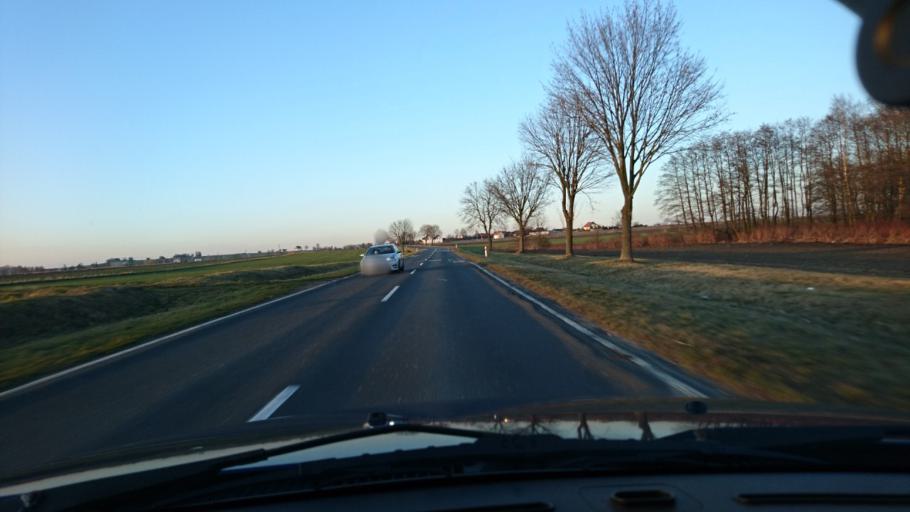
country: PL
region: Silesian Voivodeship
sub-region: Powiat gliwicki
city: Wielowies
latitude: 50.4640
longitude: 18.6110
